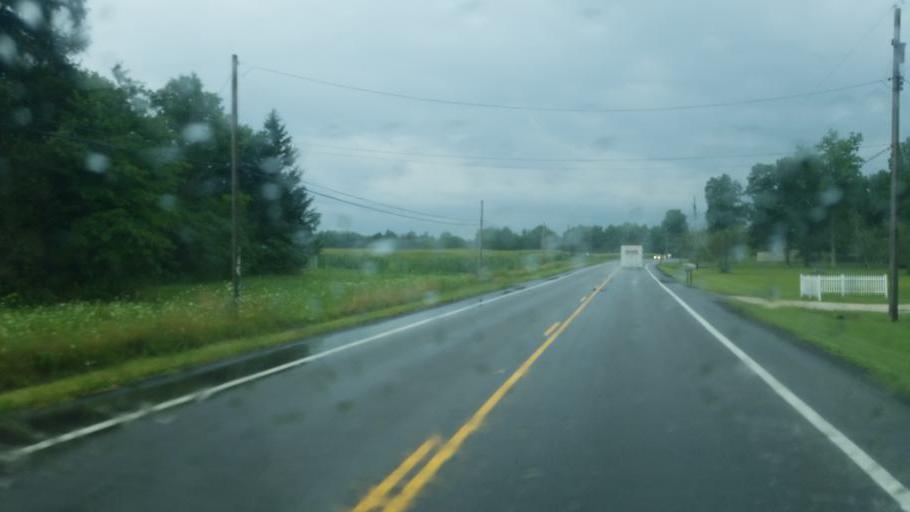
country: US
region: Ohio
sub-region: Trumbull County
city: Champion Heights
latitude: 41.3530
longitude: -80.8593
